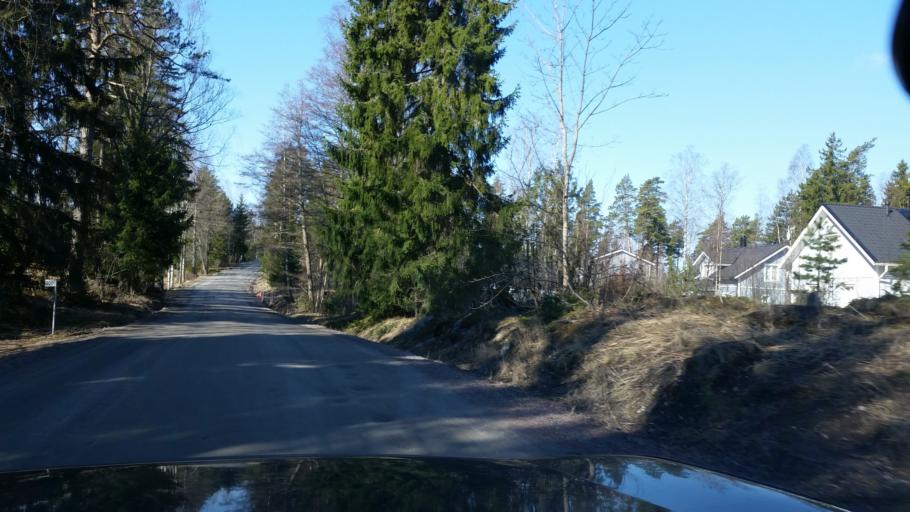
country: FI
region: Uusimaa
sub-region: Raaseporin
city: Inga
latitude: 60.0472
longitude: 23.9593
